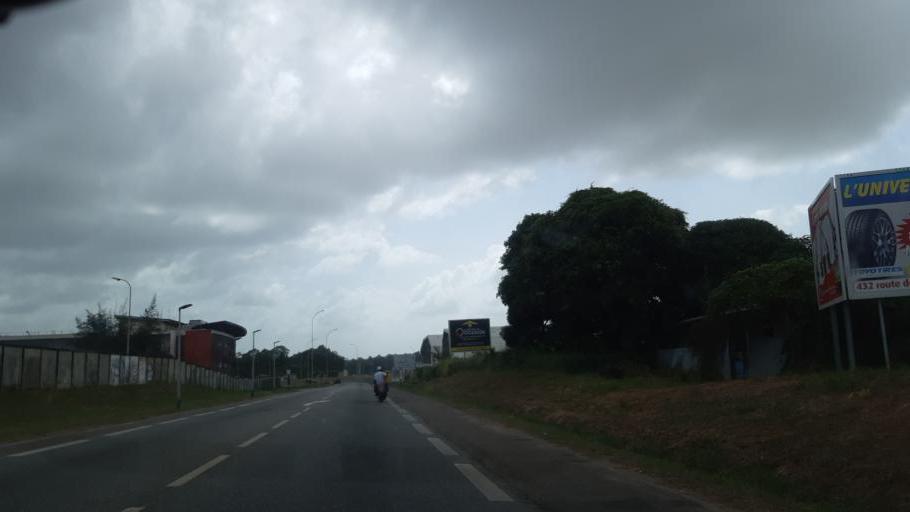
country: GF
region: Guyane
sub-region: Guyane
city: Cayenne
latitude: 4.9261
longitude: -52.3215
